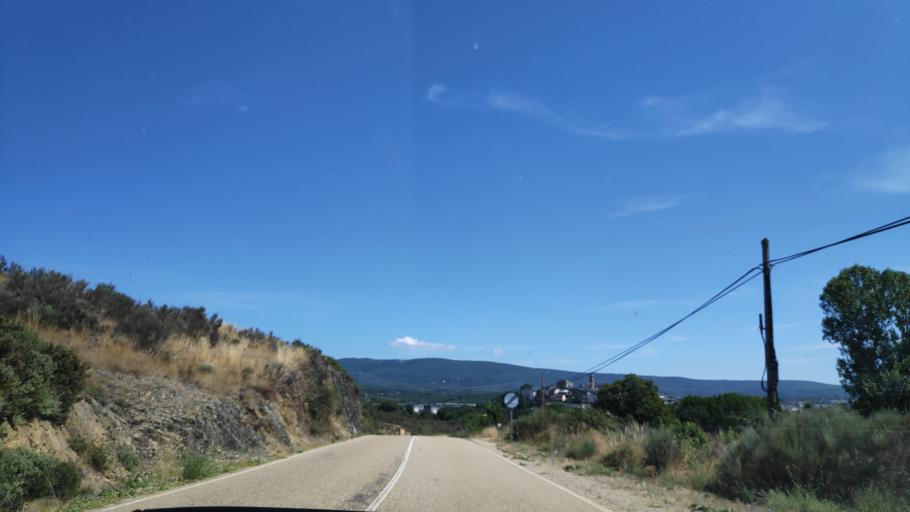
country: ES
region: Castille and Leon
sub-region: Provincia de Zamora
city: Puebla de Sanabria
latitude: 42.0492
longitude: -6.6431
